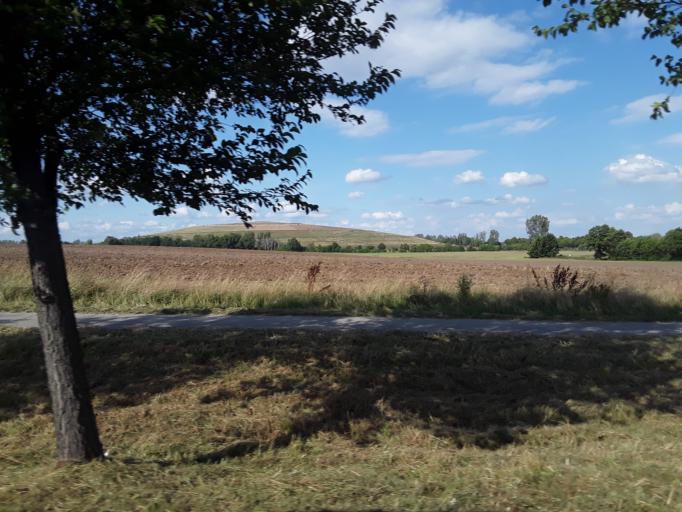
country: DE
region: Berlin
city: Buch
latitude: 52.6265
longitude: 13.5380
